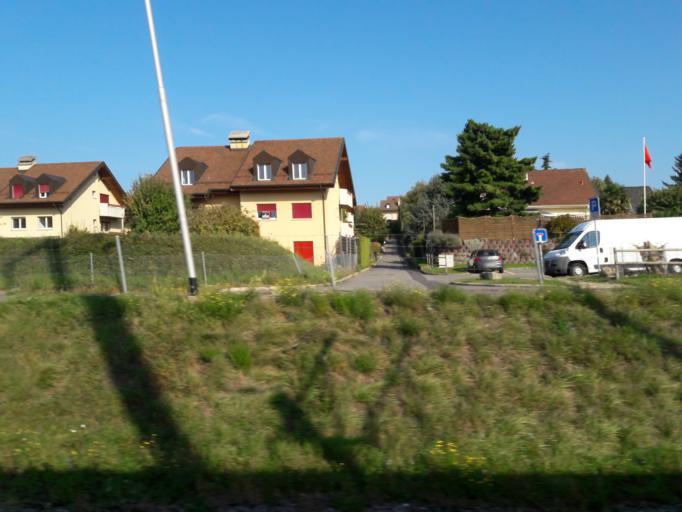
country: CH
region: Vaud
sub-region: Morges District
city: Saint-Prex
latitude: 46.4778
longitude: 6.4453
